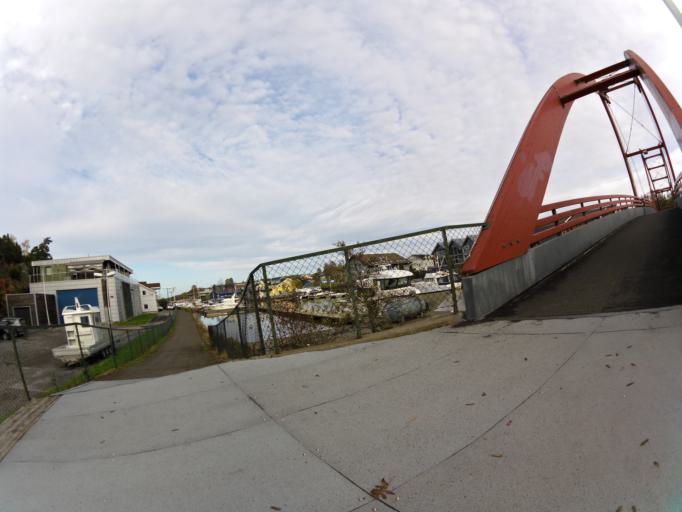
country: NO
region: Ostfold
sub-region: Fredrikstad
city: Fredrikstad
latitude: 59.2226
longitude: 10.9143
